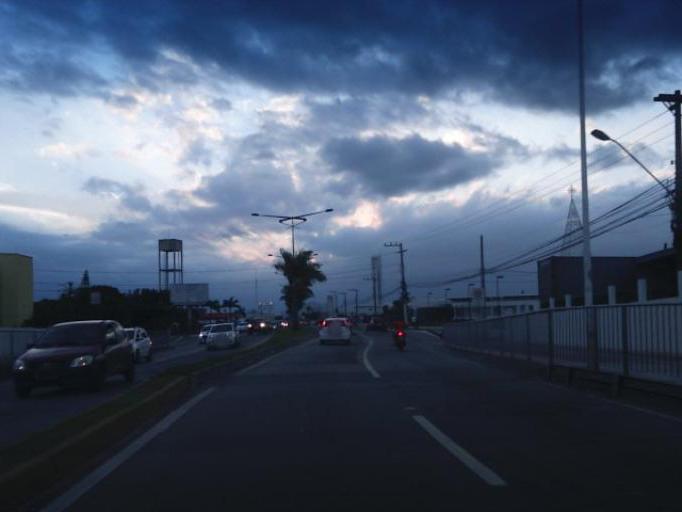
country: BR
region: Santa Catarina
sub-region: Itajai
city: Itajai
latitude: -26.9107
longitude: -48.6851
